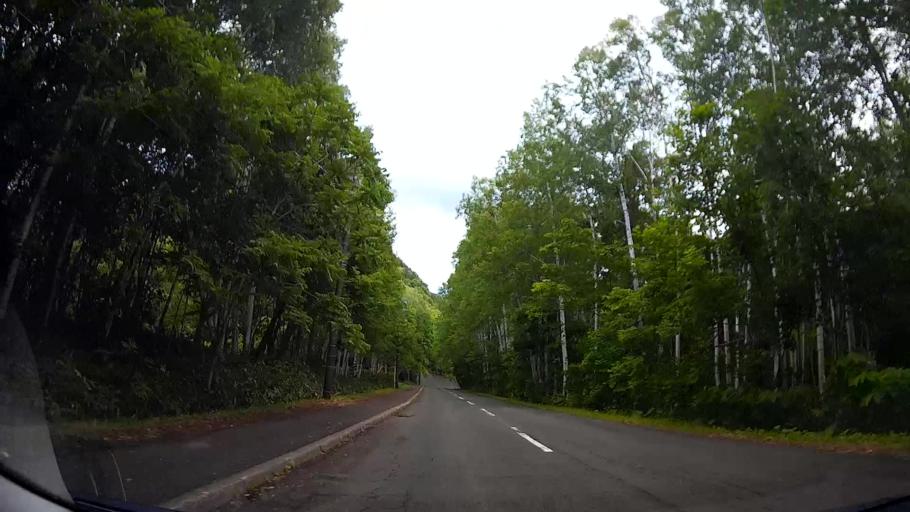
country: JP
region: Hokkaido
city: Sapporo
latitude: 42.9351
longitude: 141.1536
